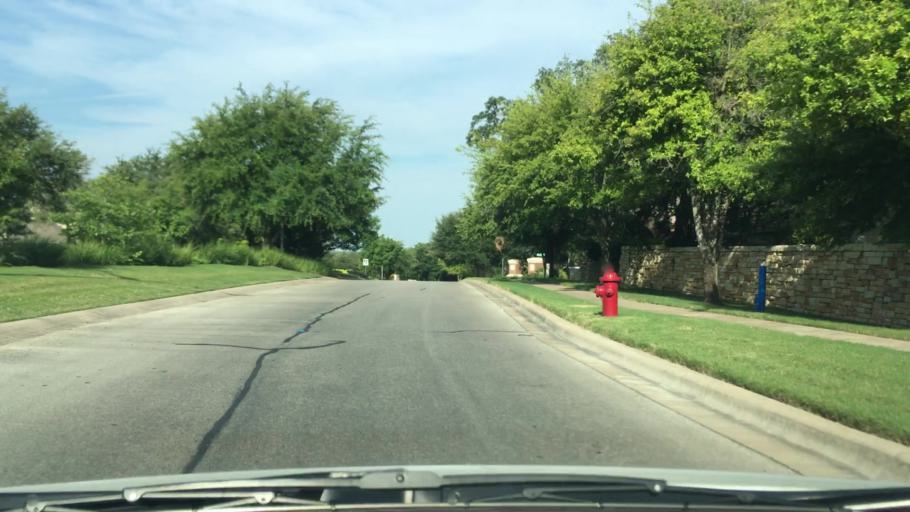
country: US
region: Texas
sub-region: Williamson County
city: Anderson Mill
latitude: 30.4687
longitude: -97.8469
